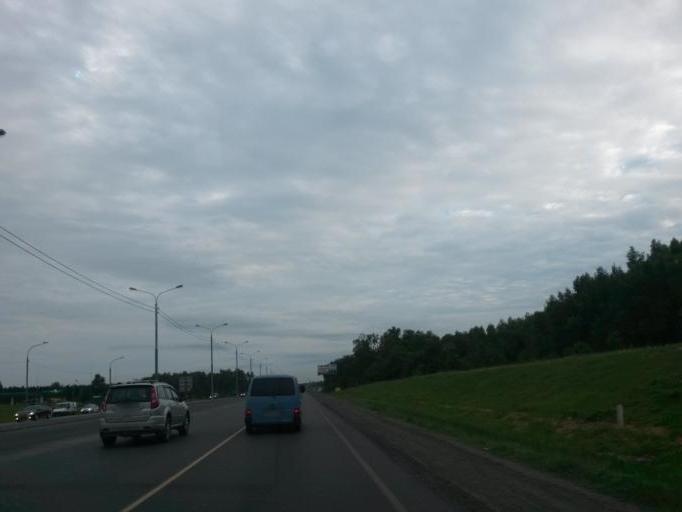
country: RU
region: Moskovskaya
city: L'vovskiy
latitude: 55.3202
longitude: 37.5579
